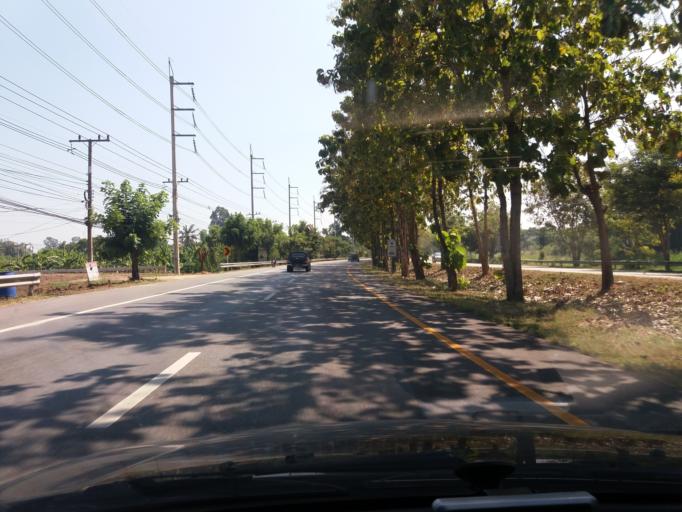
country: TH
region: Chai Nat
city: Chai Nat
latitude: 15.1233
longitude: 100.1490
